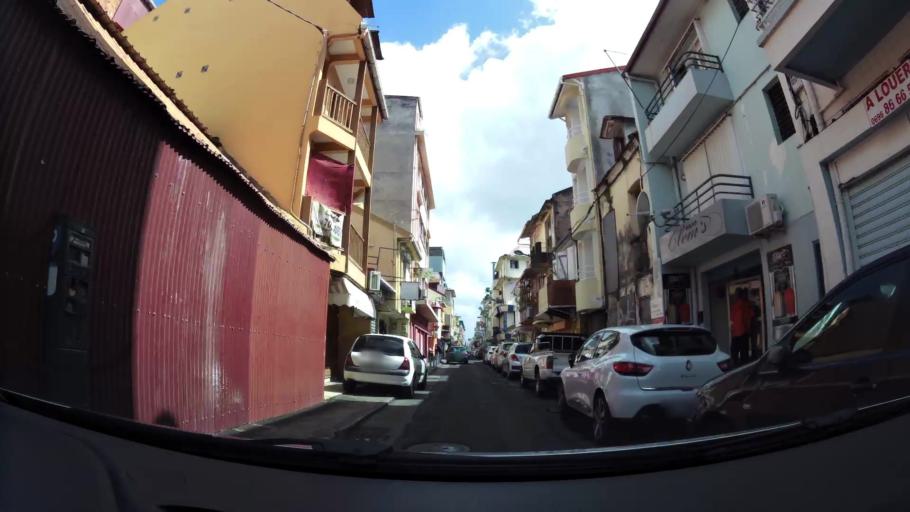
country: MQ
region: Martinique
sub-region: Martinique
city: Fort-de-France
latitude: 14.6068
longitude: -61.0729
